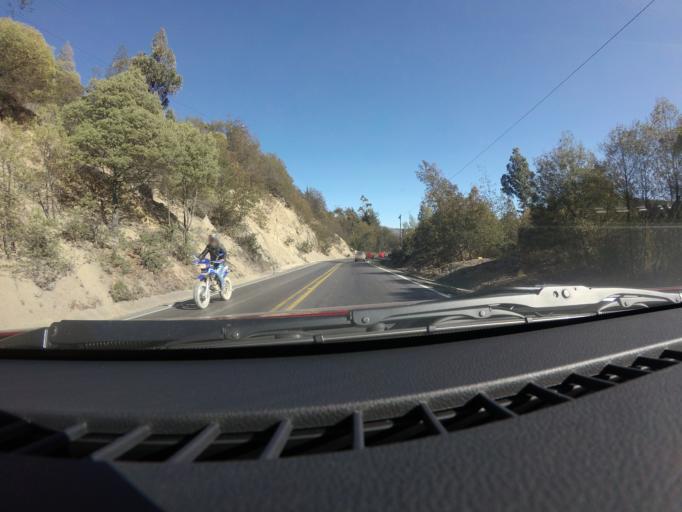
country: CO
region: Cundinamarca
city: Sutatausa
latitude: 5.2338
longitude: -73.8558
